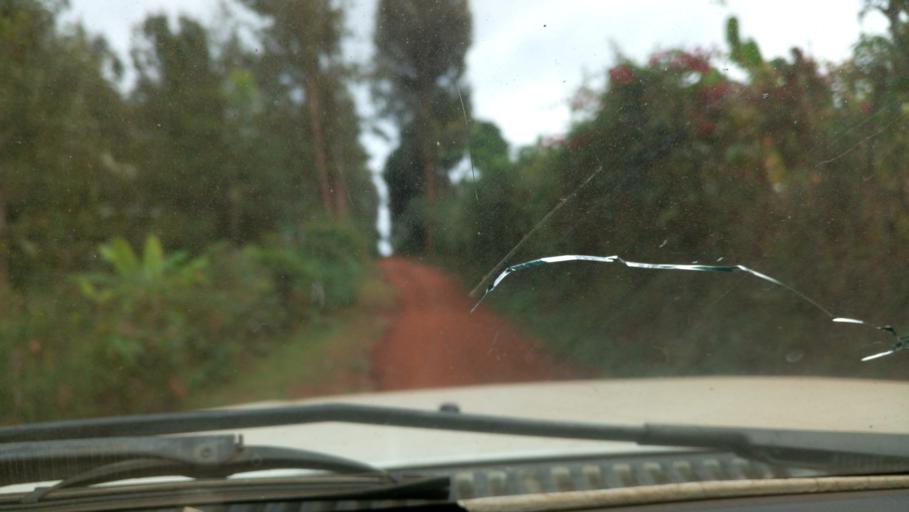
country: KE
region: Murang'a District
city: Maragua
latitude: -0.8370
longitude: 37.0473
